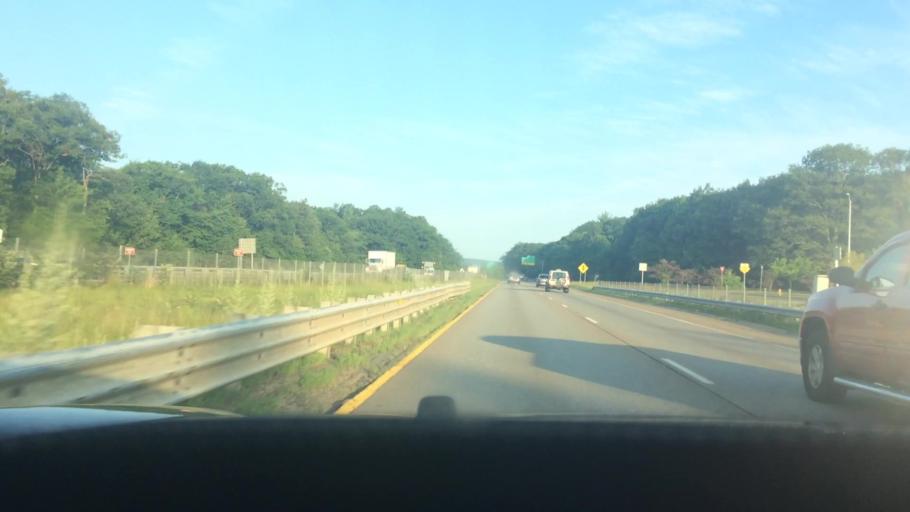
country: US
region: Massachusetts
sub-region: Middlesex County
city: Shirley
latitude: 42.5210
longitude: -71.7012
